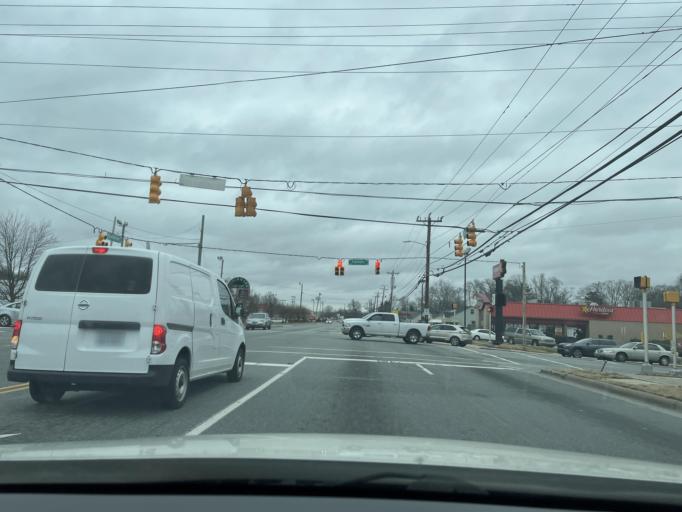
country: US
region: North Carolina
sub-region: Guilford County
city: Greensboro
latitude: 36.0149
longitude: -79.8044
